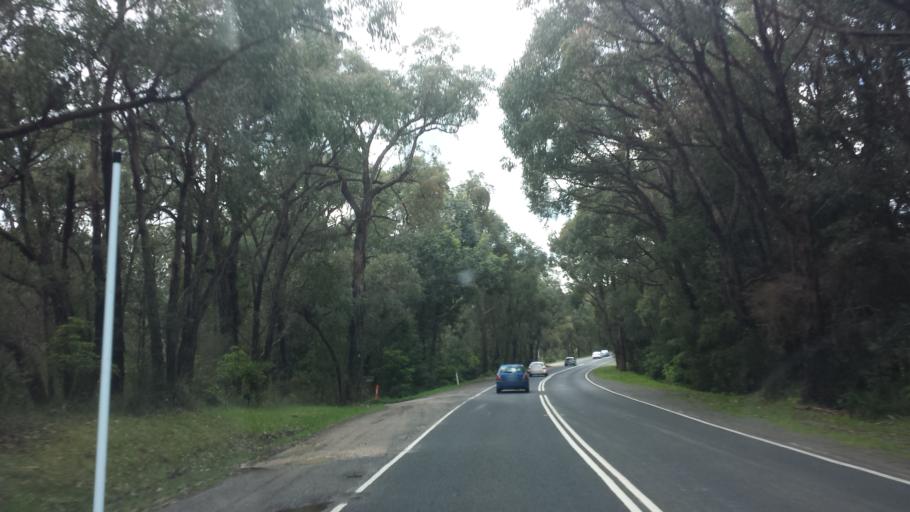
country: AU
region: Victoria
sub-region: Yarra Ranges
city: Selby
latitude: -37.9361
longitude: 145.4054
